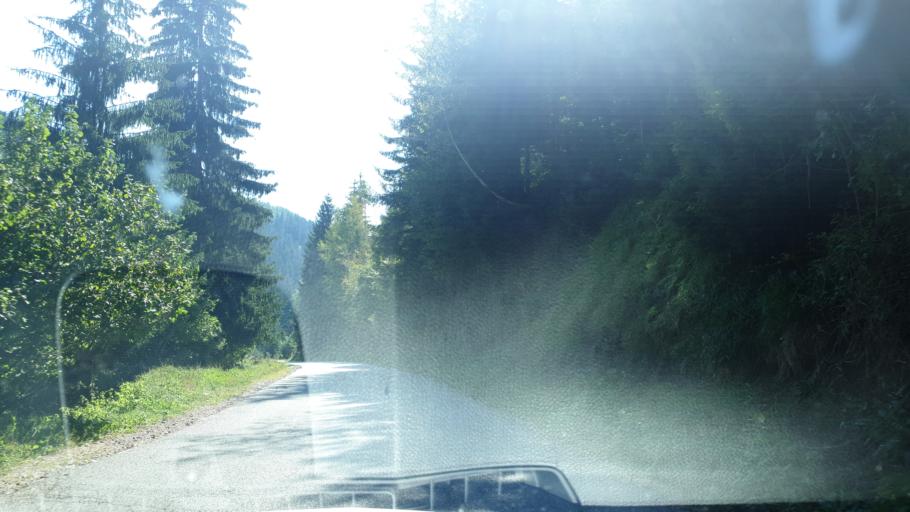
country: RS
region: Central Serbia
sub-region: Zlatiborski Okrug
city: Nova Varos
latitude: 43.4582
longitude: 19.8362
